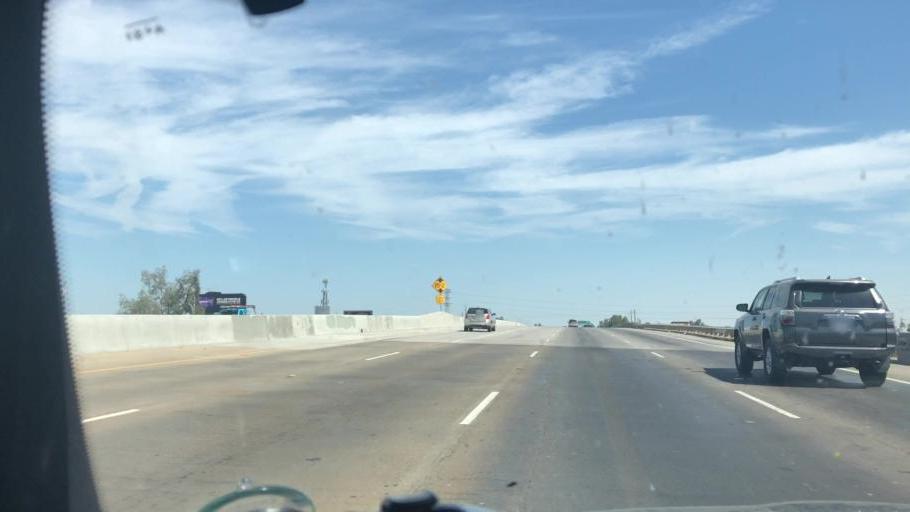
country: US
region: California
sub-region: Kern County
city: Greenfield
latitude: 35.3105
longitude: -119.0341
